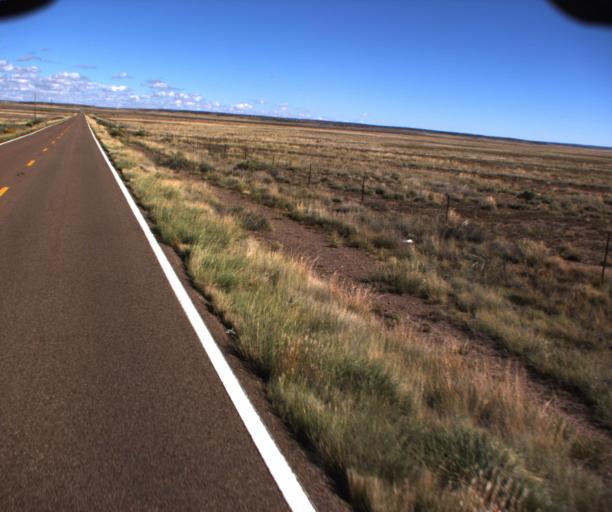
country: US
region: Arizona
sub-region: Apache County
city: Saint Johns
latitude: 34.5998
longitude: -109.3249
